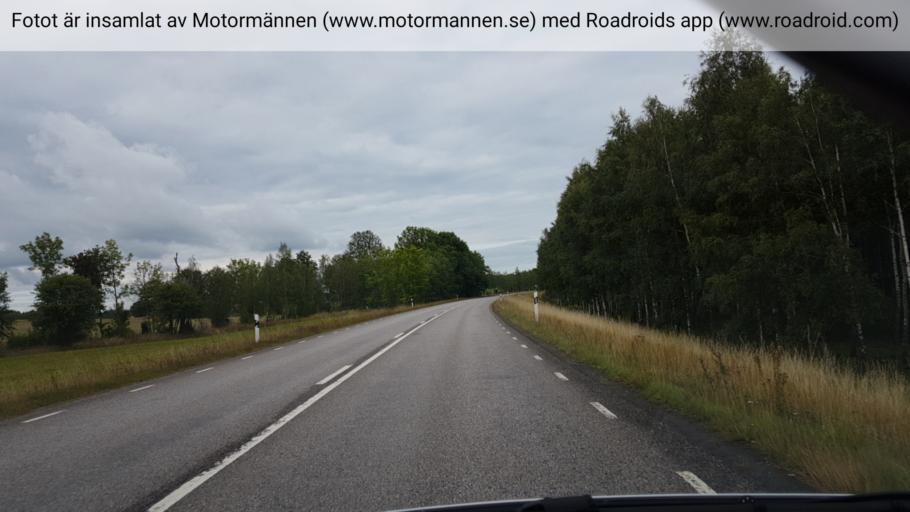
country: SE
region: Vaestra Goetaland
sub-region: Hjo Kommun
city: Hjo
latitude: 58.3161
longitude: 14.2603
